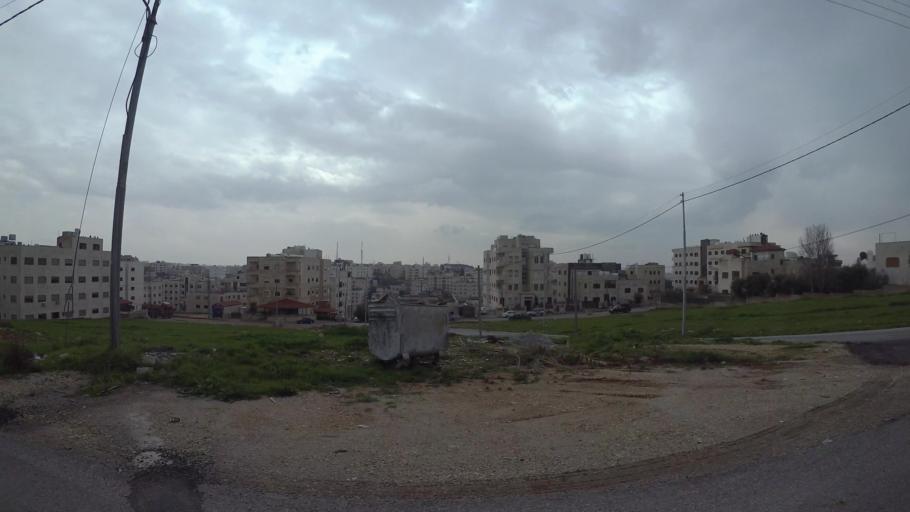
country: JO
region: Amman
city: Umm as Summaq
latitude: 31.9026
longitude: 35.8344
